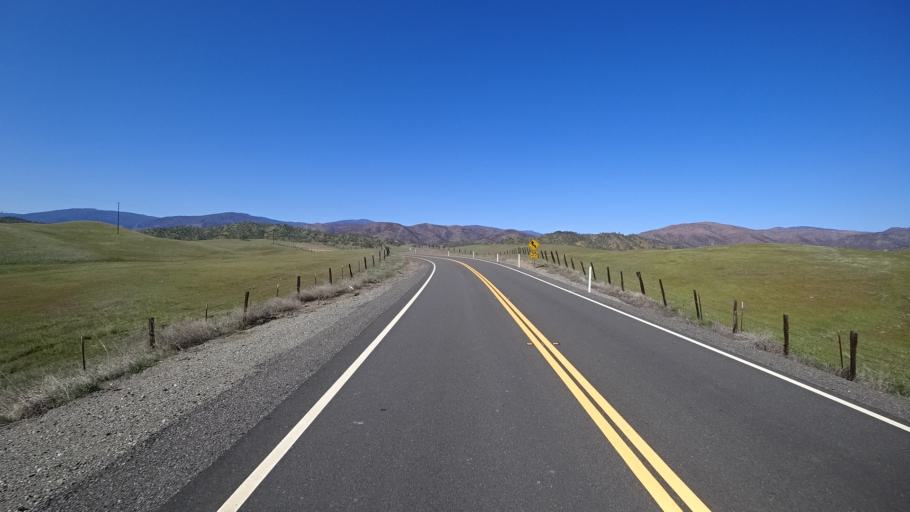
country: US
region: California
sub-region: Glenn County
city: Orland
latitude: 39.6594
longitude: -122.5490
